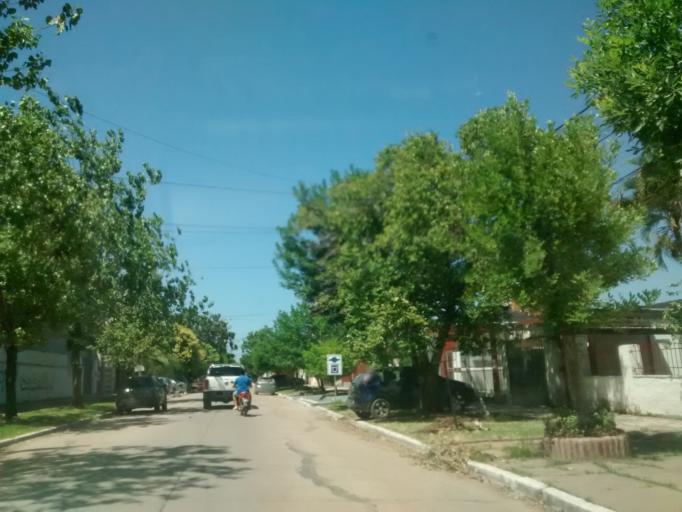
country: AR
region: Chaco
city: Resistencia
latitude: -27.4605
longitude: -58.9811
